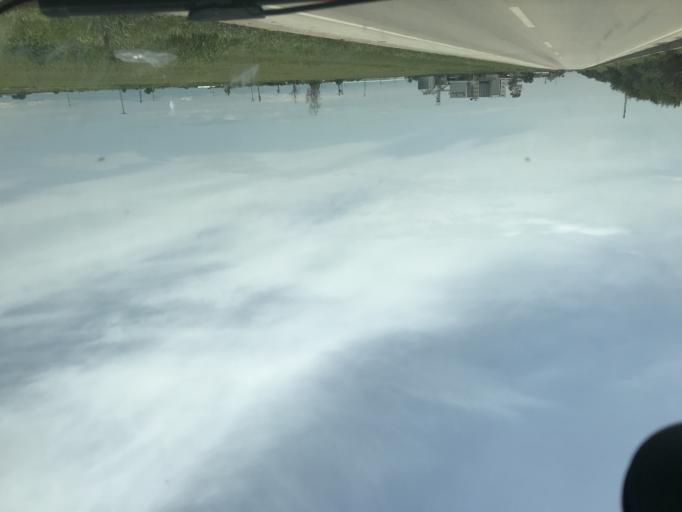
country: TR
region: Adana
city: Yakapinar
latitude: 36.9737
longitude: 35.5033
